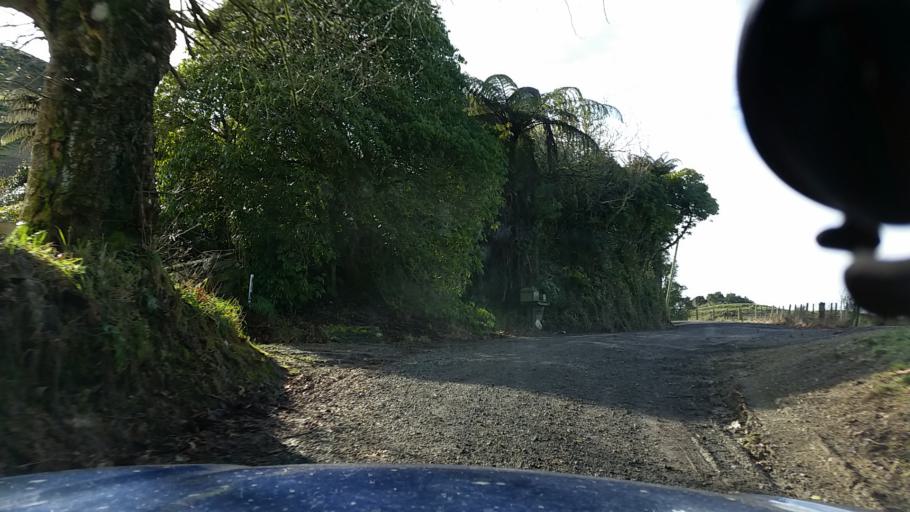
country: NZ
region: Taranaki
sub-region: New Plymouth District
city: Waitara
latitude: -39.0340
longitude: 174.7839
